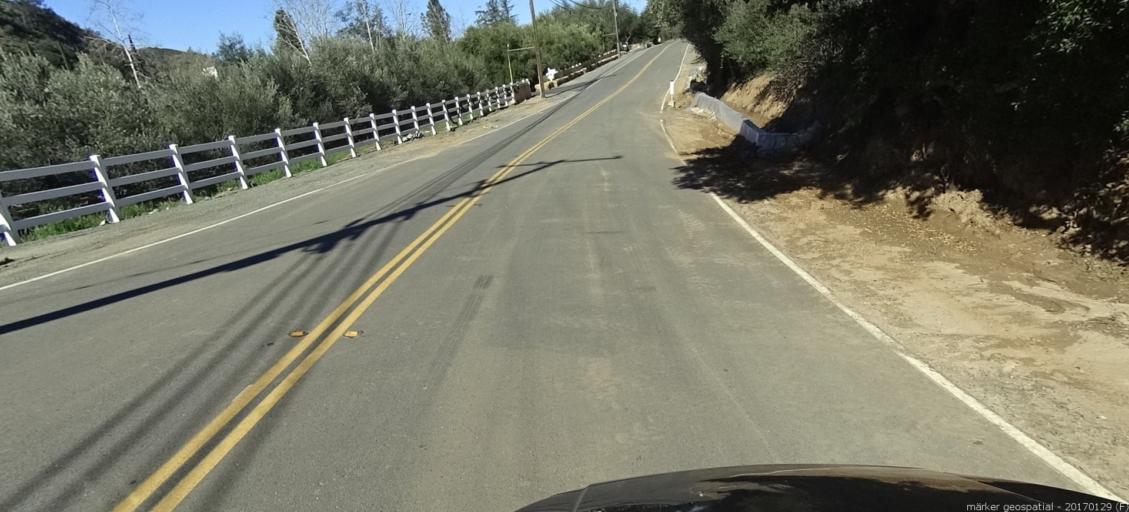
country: US
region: California
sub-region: Orange County
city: Foothill Ranch
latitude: 33.7108
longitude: -117.6394
